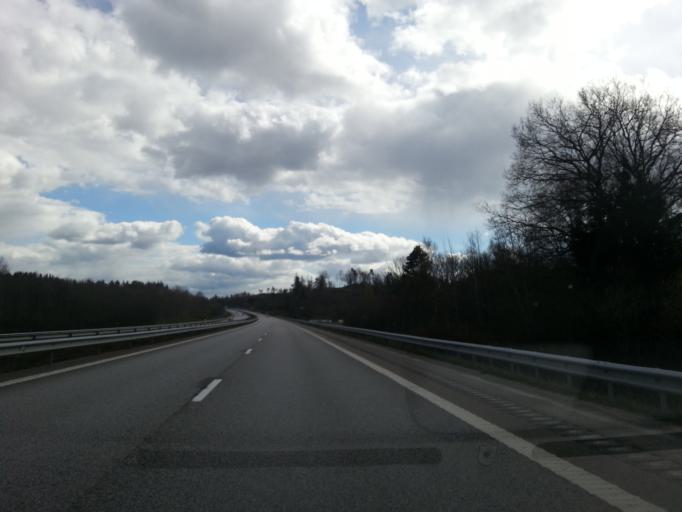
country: SE
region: Vaestra Goetaland
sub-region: Uddevalla Kommun
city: Uddevalla
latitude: 58.3070
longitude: 11.8589
